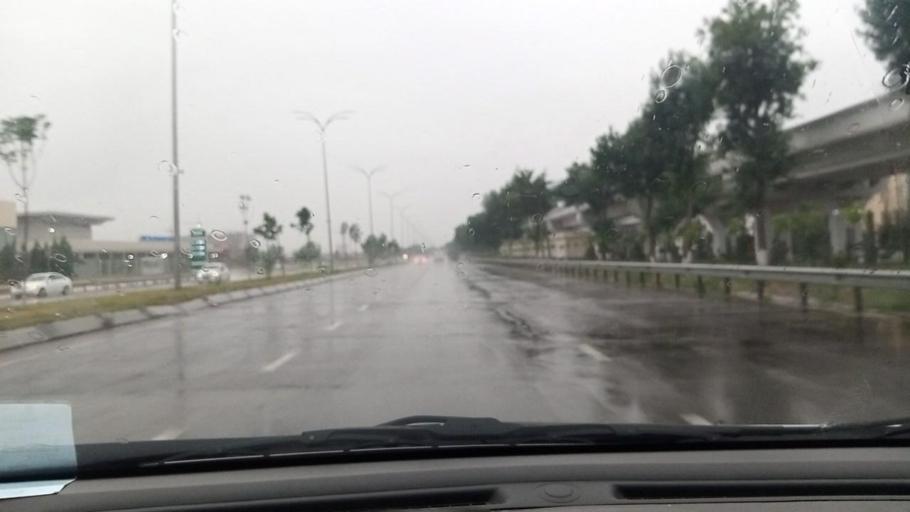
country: UZ
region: Toshkent Shahri
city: Bektemir
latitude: 41.2838
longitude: 69.3603
